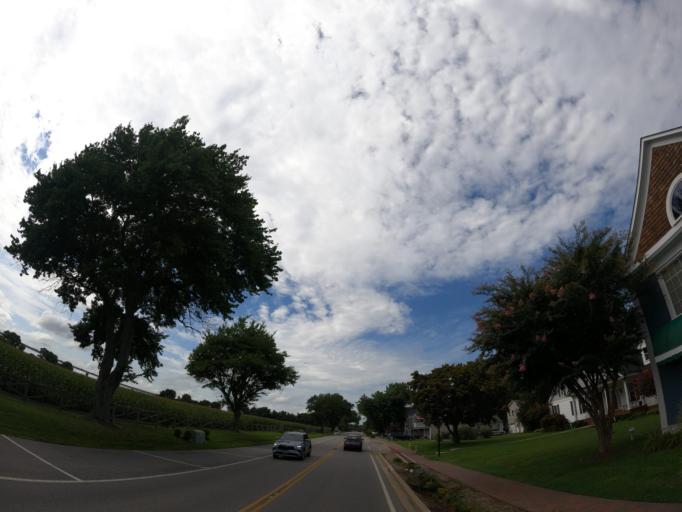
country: US
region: Maryland
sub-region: Calvert County
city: Solomons
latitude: 38.3267
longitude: -76.4623
